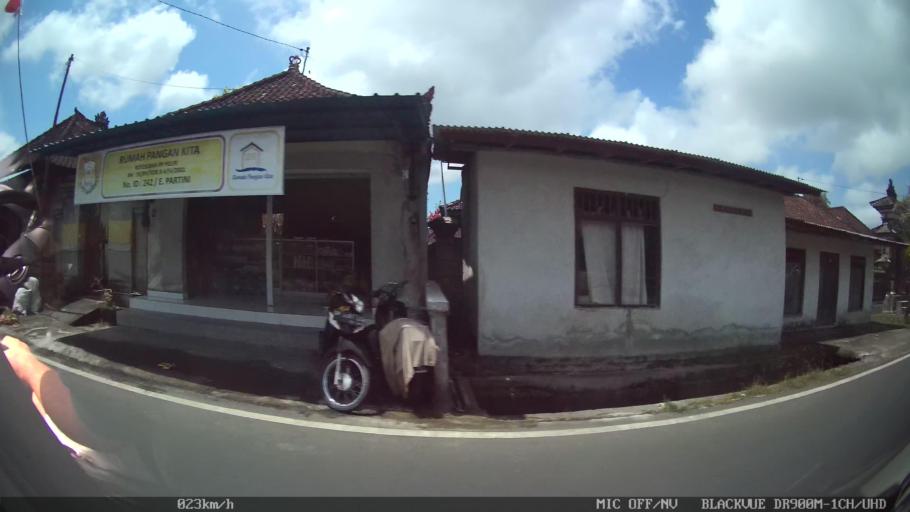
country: ID
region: Bali
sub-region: Kabupaten Gianyar
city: Ubud
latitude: -8.5301
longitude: 115.2832
